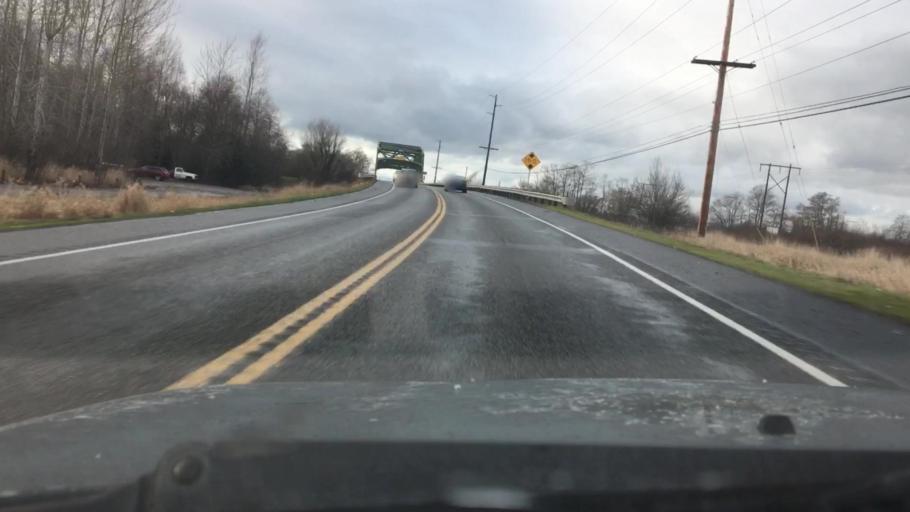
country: US
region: Washington
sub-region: Whatcom County
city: Ferndale
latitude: 48.8189
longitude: -122.5772
